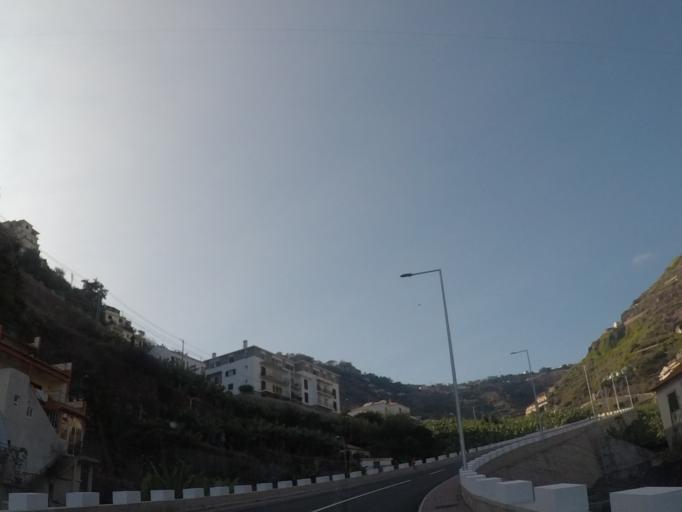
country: PT
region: Madeira
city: Camara de Lobos
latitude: 32.6562
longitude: -16.9899
